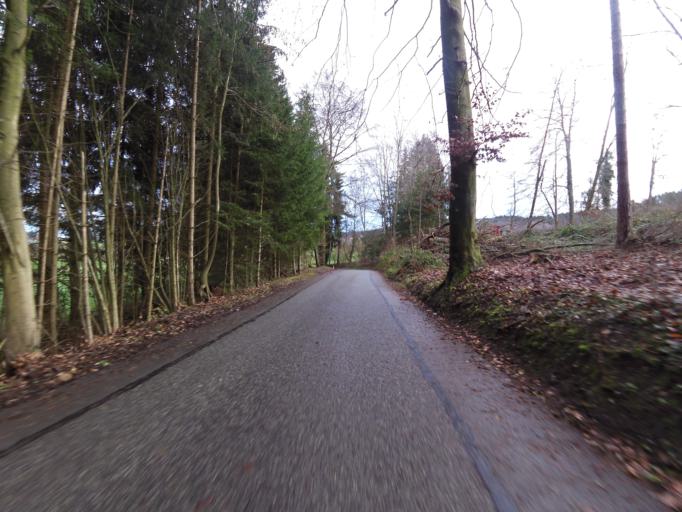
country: CH
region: Thurgau
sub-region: Frauenfeld District
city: Thundorf
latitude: 47.5539
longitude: 8.9342
